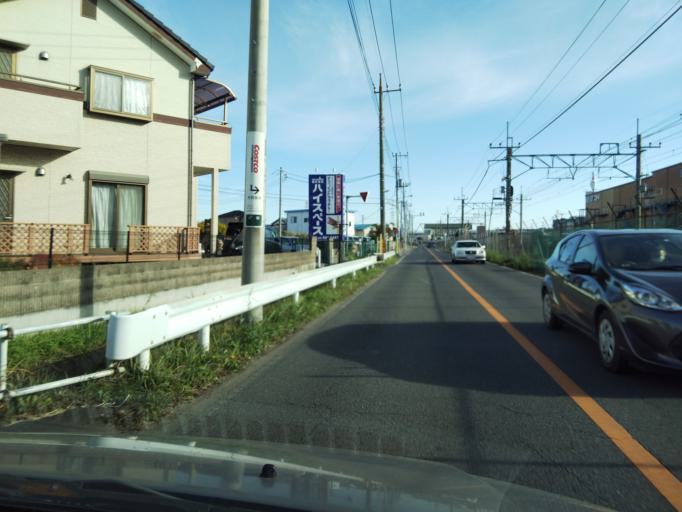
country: JP
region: Saitama
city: Yoshikawa
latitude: 35.8614
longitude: 139.8664
